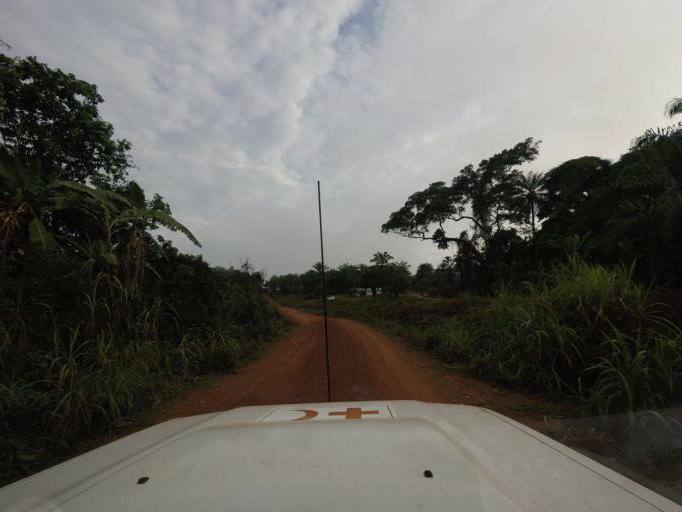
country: GN
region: Nzerekore
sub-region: Yomou
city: Yomou
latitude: 7.6898
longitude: -9.4251
